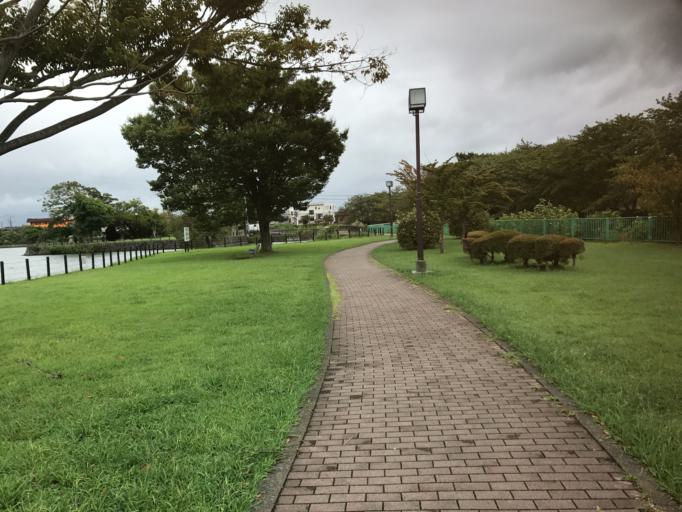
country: JP
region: Shizuoka
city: Numazu
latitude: 35.1289
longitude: 138.8796
